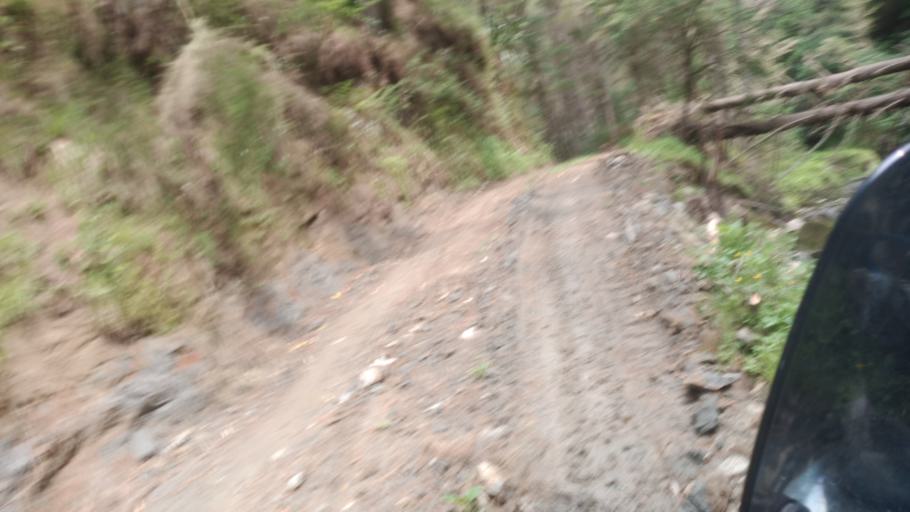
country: NZ
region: Gisborne
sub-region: Gisborne District
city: Gisborne
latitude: -38.4570
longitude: 177.9263
